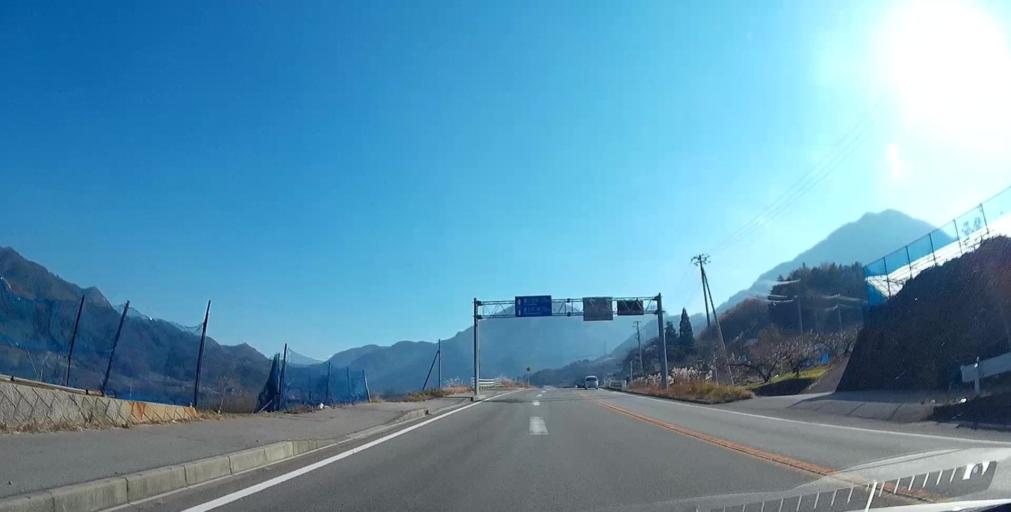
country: JP
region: Yamanashi
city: Isawa
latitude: 35.6089
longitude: 138.7015
